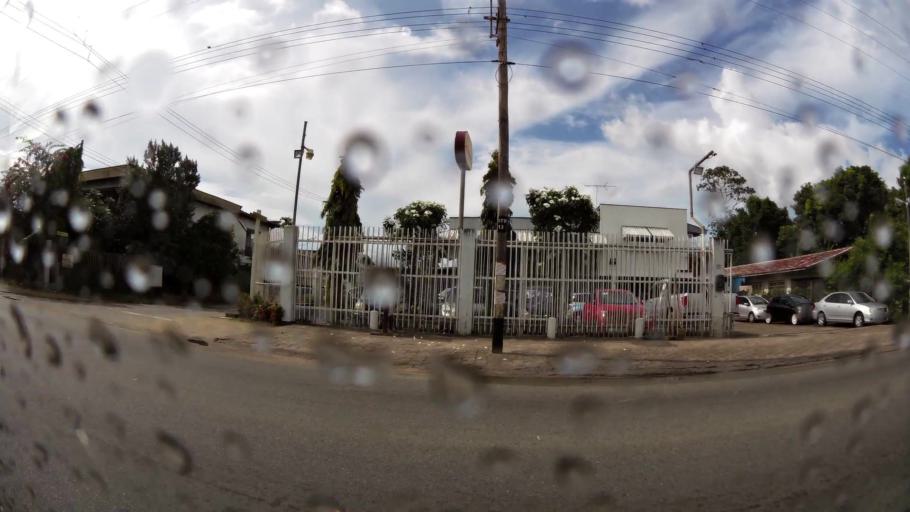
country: SR
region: Paramaribo
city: Paramaribo
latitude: 5.8420
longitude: -55.2005
